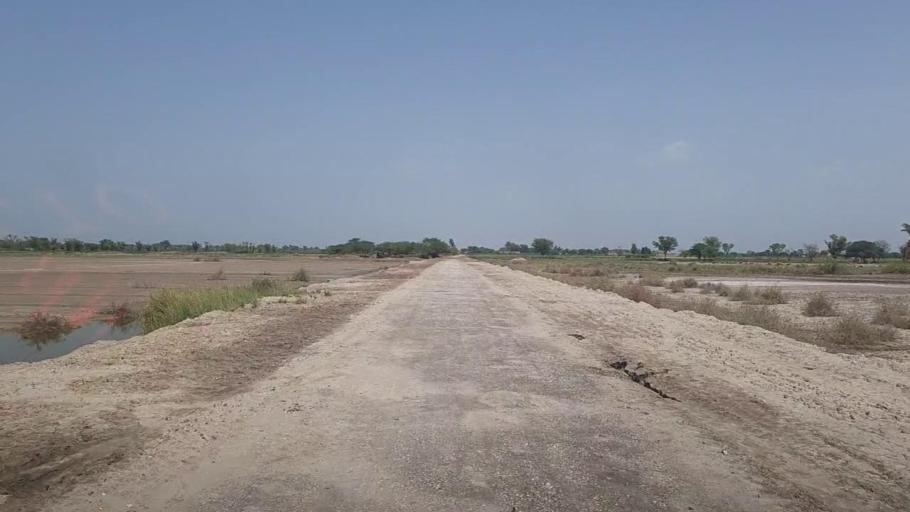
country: PK
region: Sindh
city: Pad Idan
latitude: 26.8444
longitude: 68.3149
